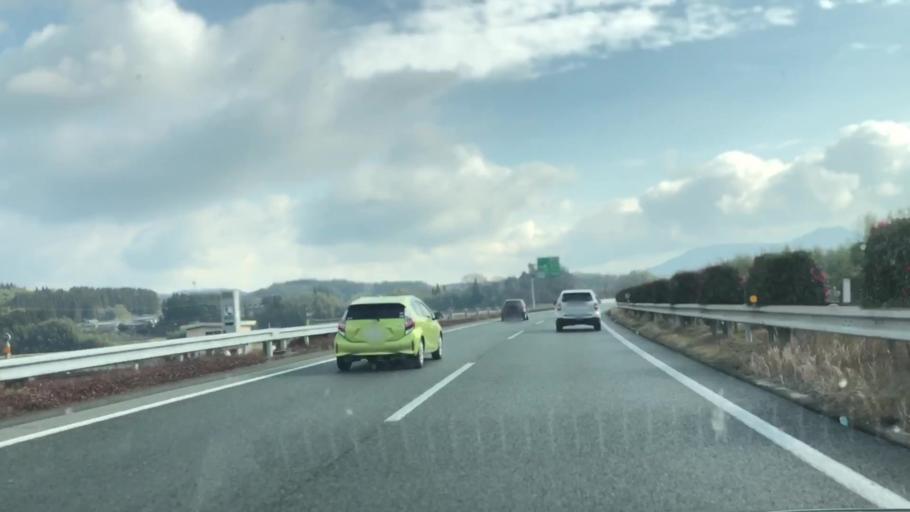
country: JP
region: Kumamoto
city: Tamana
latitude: 32.9941
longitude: 130.6000
